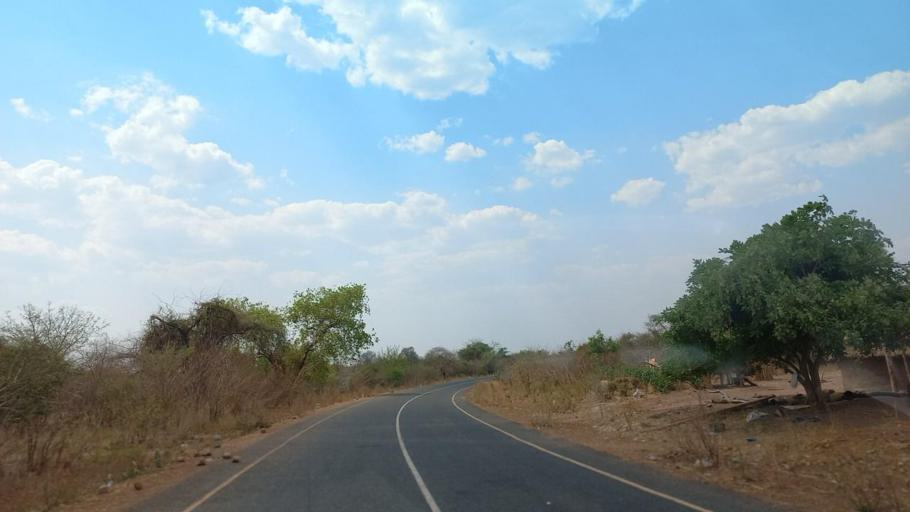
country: ZM
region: Lusaka
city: Luangwa
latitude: -15.3362
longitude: 30.3538
